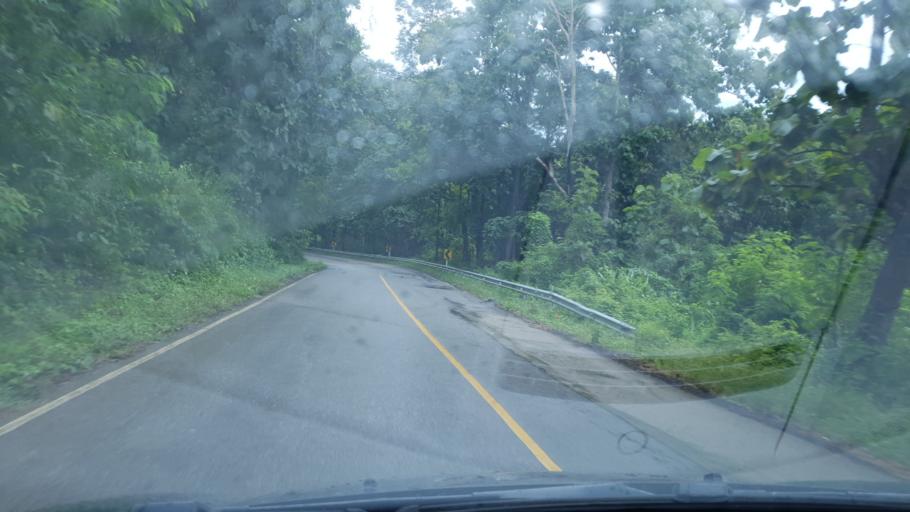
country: TH
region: Mae Hong Son
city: Pa Pae
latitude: 18.2765
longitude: 97.9391
